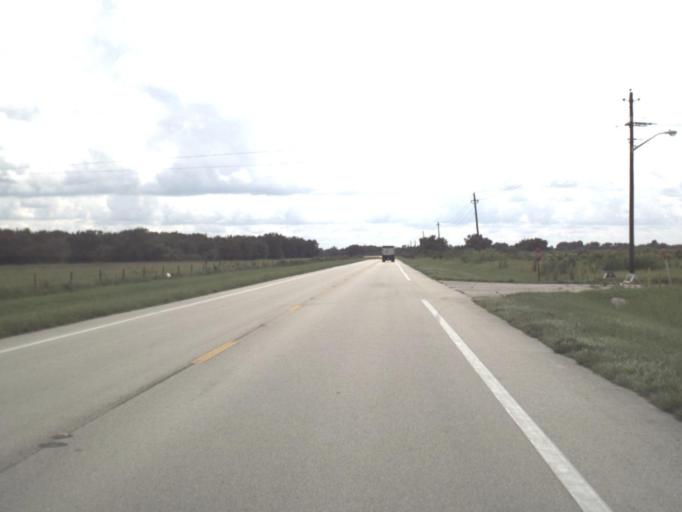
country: US
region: Florida
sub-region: DeSoto County
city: Southeast Arcadia
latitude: 27.1332
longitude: -81.7962
